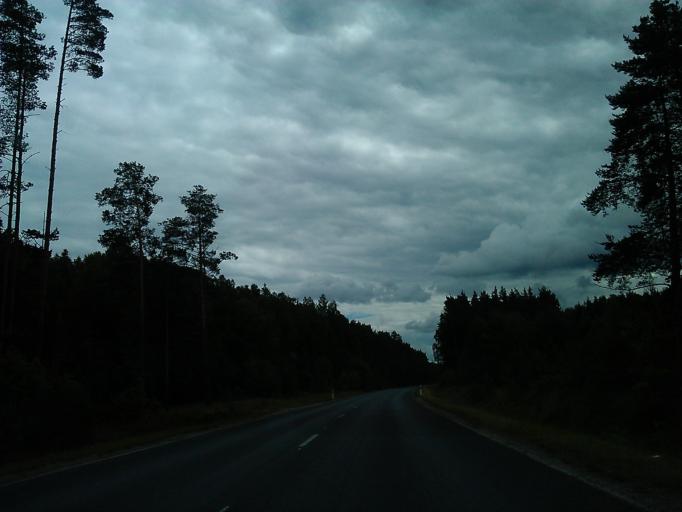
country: LV
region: Dobeles Rajons
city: Dobele
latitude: 56.6560
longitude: 23.1887
